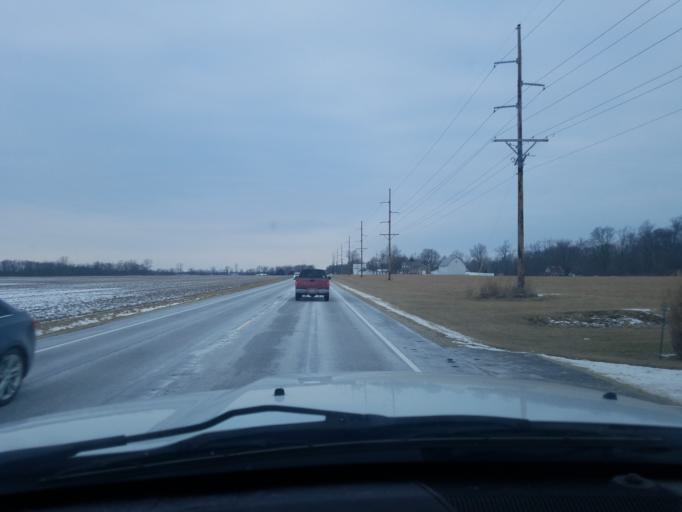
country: US
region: Indiana
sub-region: Randolph County
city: Farmland
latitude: 40.1713
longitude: -85.1010
